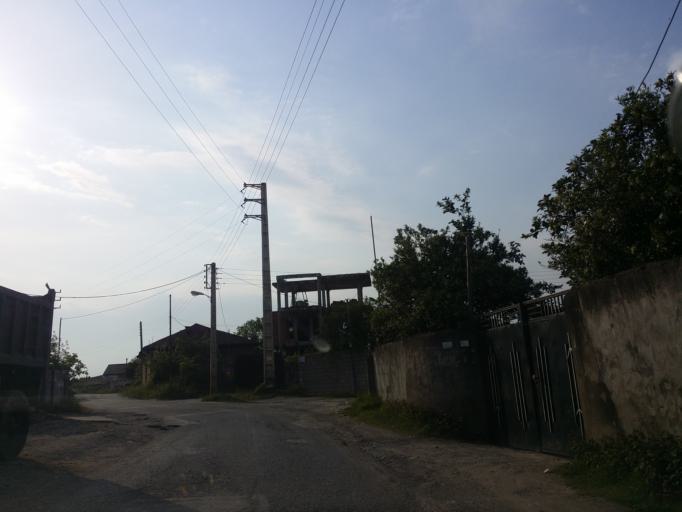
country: IR
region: Mazandaran
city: Chalus
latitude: 36.6654
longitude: 51.3745
